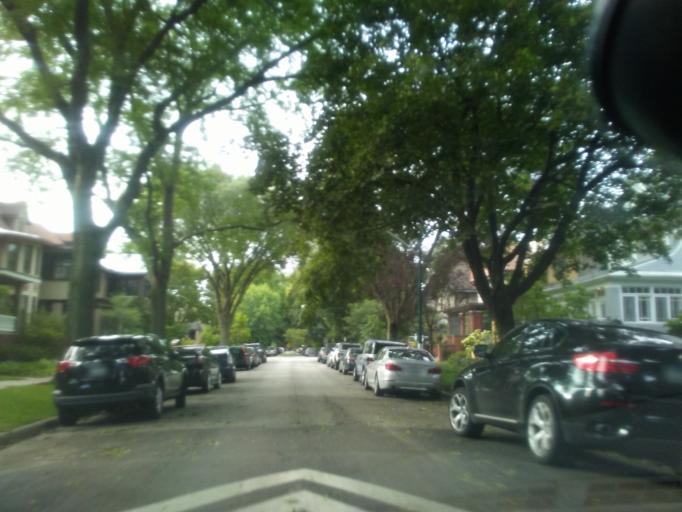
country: US
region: Illinois
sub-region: Cook County
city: Evanston
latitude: 41.9825
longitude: -87.6637
